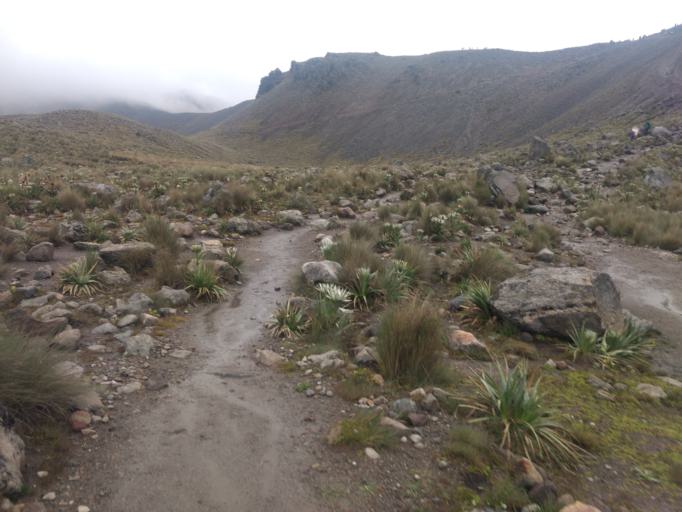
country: MX
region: Mexico
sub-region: Tenango del Valle
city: Santa Cruz Pueblo Nuevo (Pueblo Nuevo)
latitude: 19.1098
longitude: -99.7528
